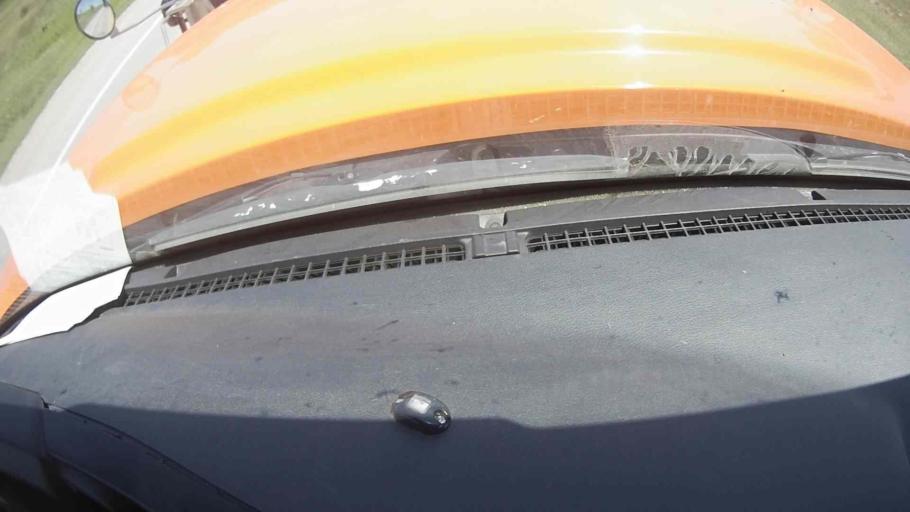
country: US
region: Iowa
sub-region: Mahaska County
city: Oskaloosa
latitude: 41.2943
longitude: -92.6846
